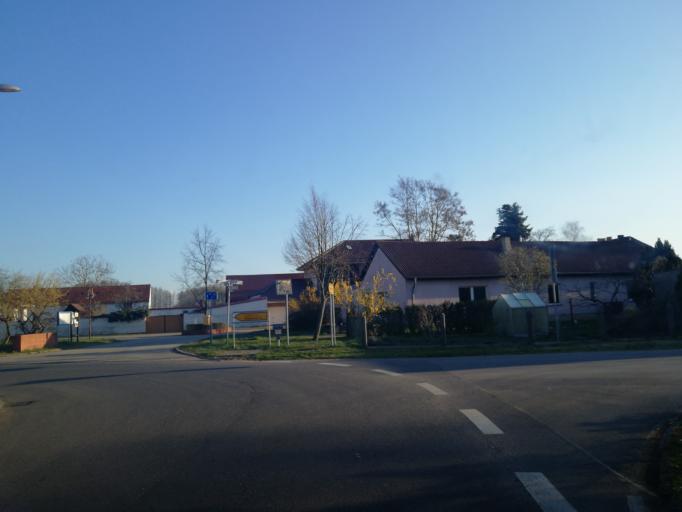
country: DE
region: Brandenburg
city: Luckau
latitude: 51.8206
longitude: 13.6480
